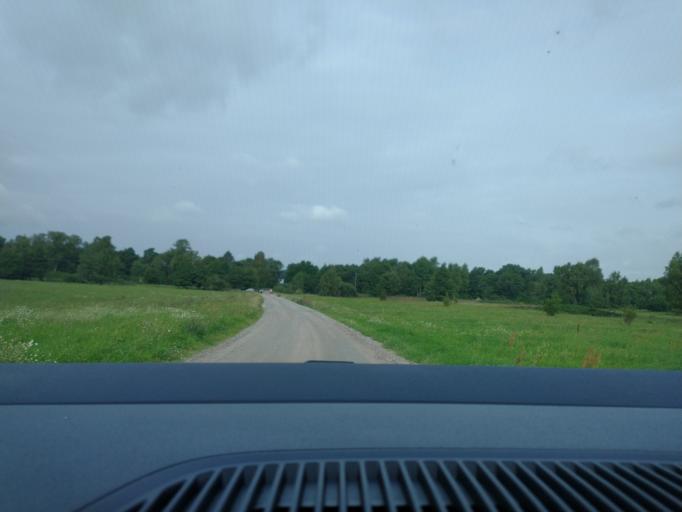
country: SE
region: Skane
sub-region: Lunds Kommun
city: Veberod
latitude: 55.6887
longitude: 13.4974
